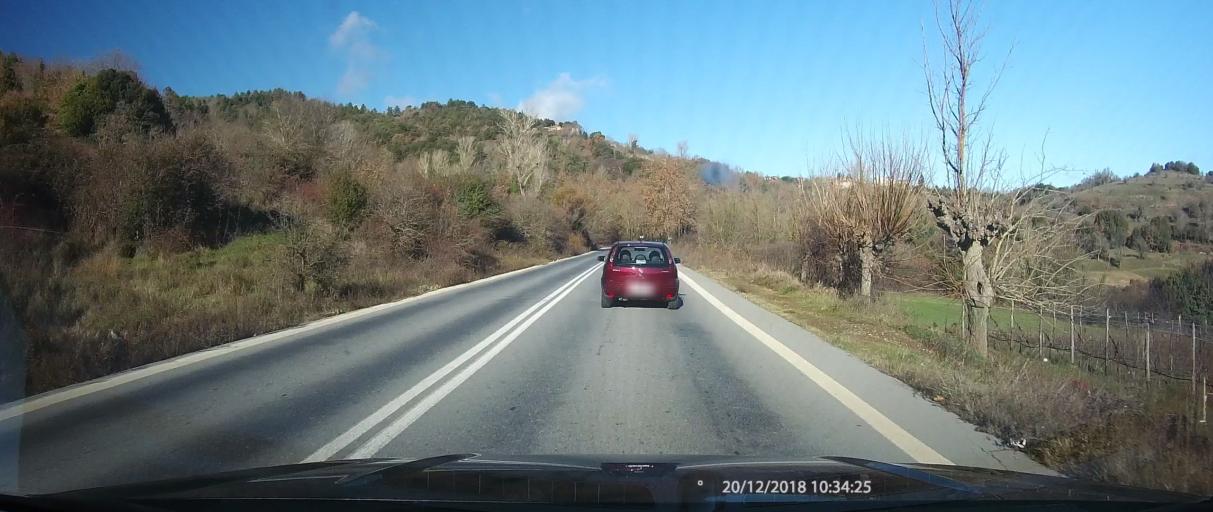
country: GR
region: Peloponnese
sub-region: Nomos Lakonias
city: Kariai
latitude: 37.3497
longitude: 22.4116
